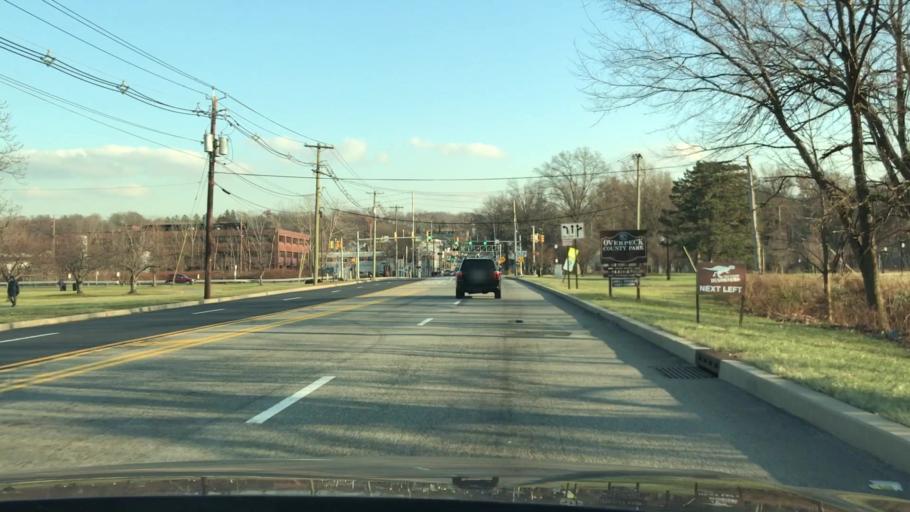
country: US
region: New Jersey
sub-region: Bergen County
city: Leonia
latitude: 40.8658
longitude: -73.9968
